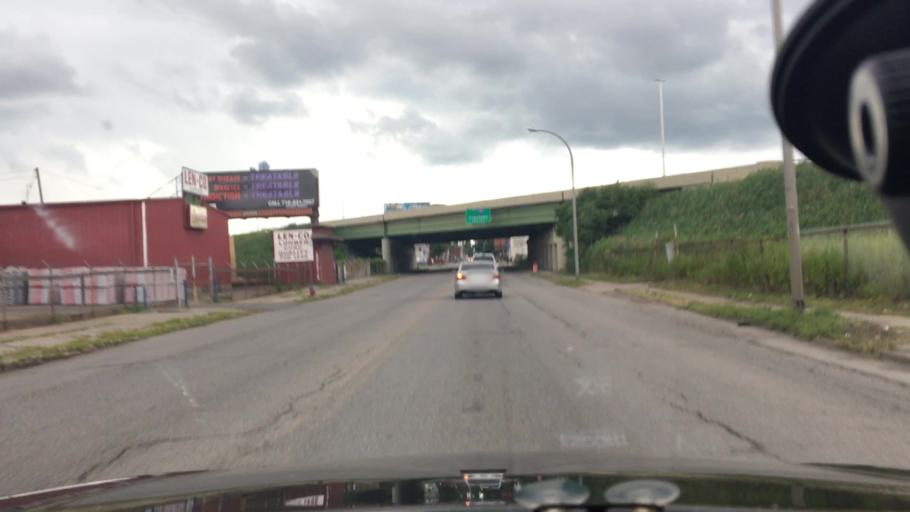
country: US
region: New York
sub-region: Erie County
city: West Seneca
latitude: 42.8675
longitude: -78.8262
